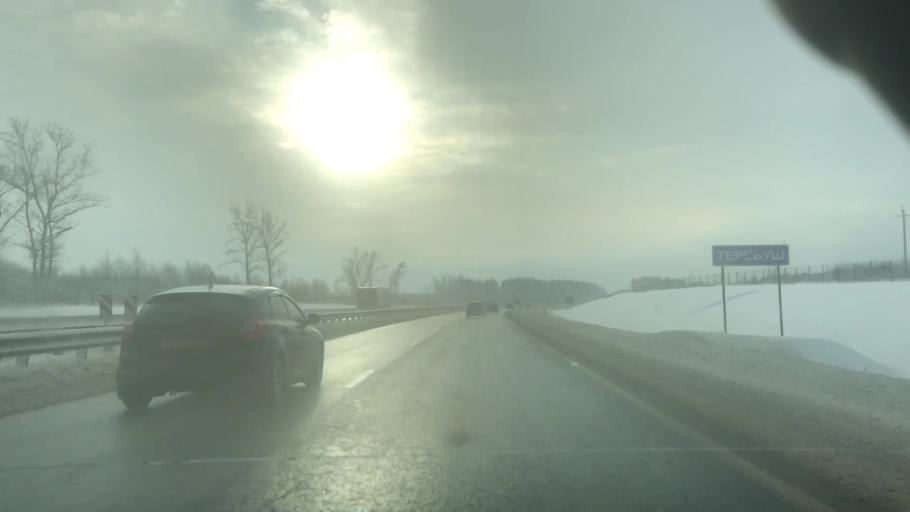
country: RU
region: Tula
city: Venev
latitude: 54.2741
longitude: 38.1601
